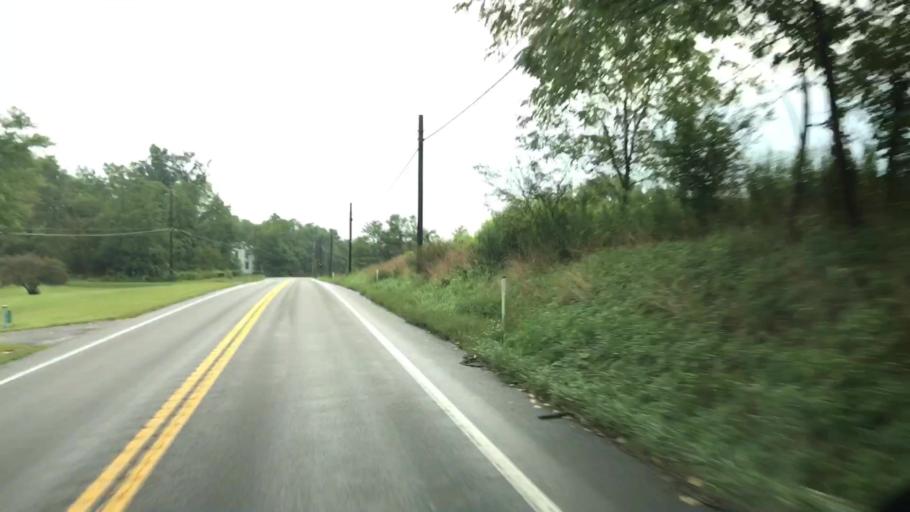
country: US
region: Pennsylvania
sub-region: Perry County
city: New Bloomfield
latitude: 40.3767
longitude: -77.1527
